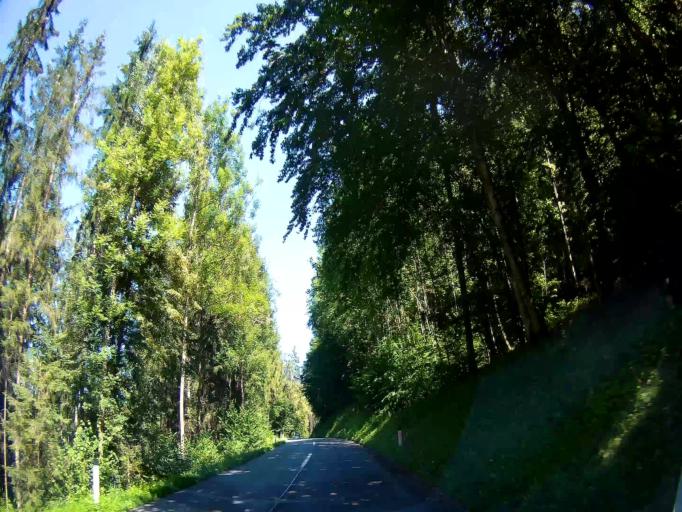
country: AT
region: Carinthia
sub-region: Politischer Bezirk Klagenfurt Land
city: Grafenstein
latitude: 46.6028
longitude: 14.4224
